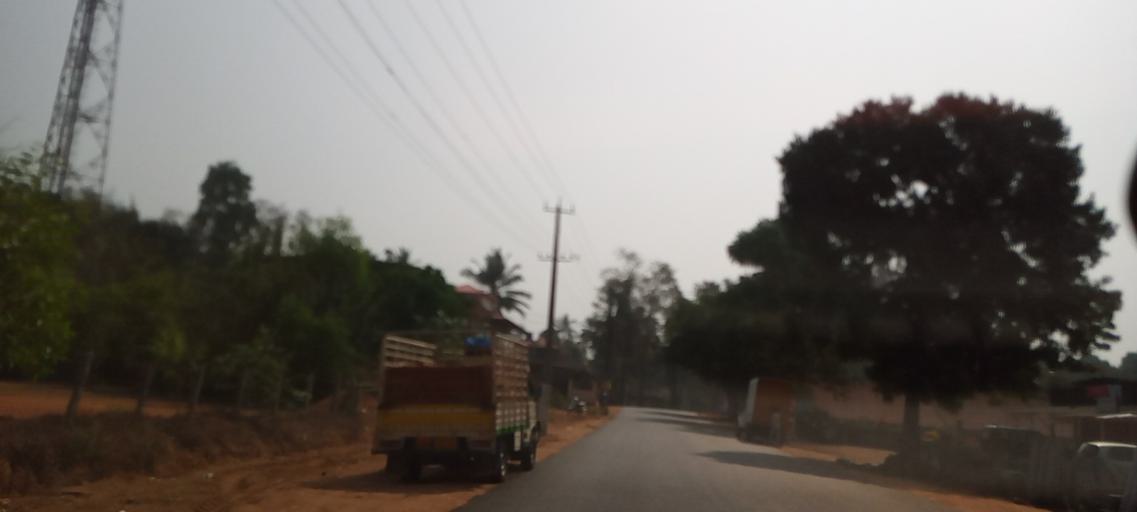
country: IN
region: Karnataka
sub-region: Udupi
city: Someshwar
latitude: 13.5273
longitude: 74.9244
